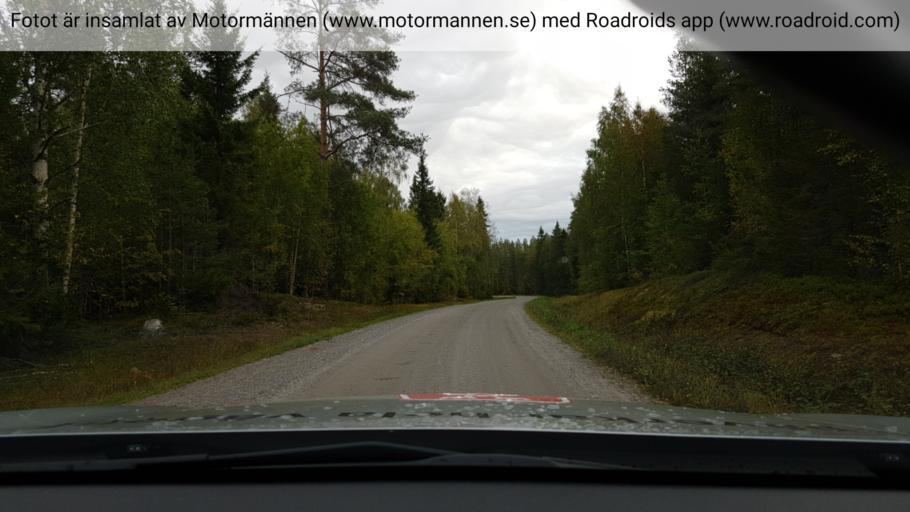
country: SE
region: Vaesterbotten
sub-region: Skelleftea Kommun
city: Byske
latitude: 65.1065
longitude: 21.1798
